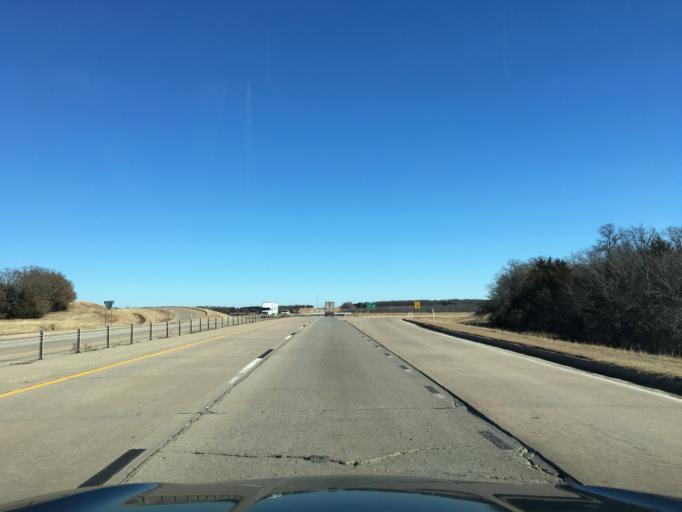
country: US
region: Oklahoma
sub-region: Pawnee County
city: Pawnee
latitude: 36.2248
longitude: -96.7906
